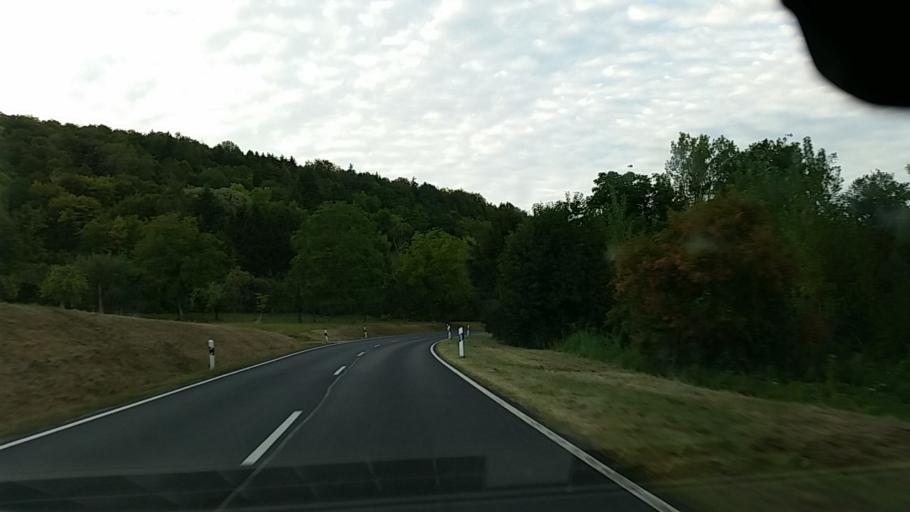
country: DE
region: Bavaria
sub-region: Regierungsbezirk Unterfranken
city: Himmelstadt
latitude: 49.9072
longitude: 9.8015
